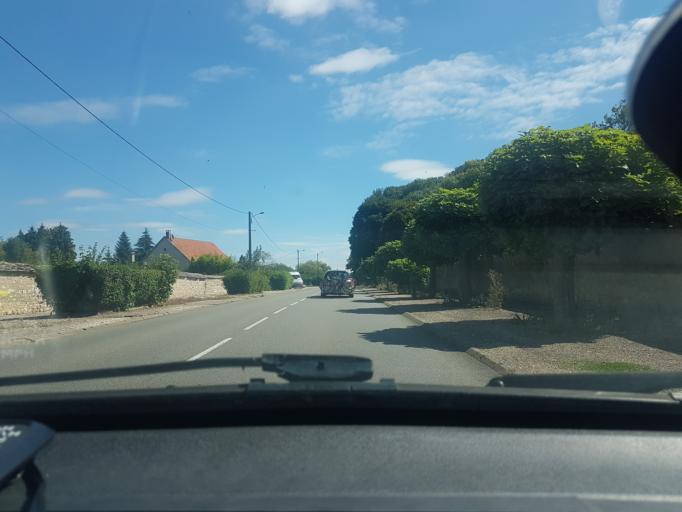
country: FR
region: Bourgogne
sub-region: Departement de la Cote-d'Or
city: Mirebeau-sur-Beze
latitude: 47.4025
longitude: 5.4061
